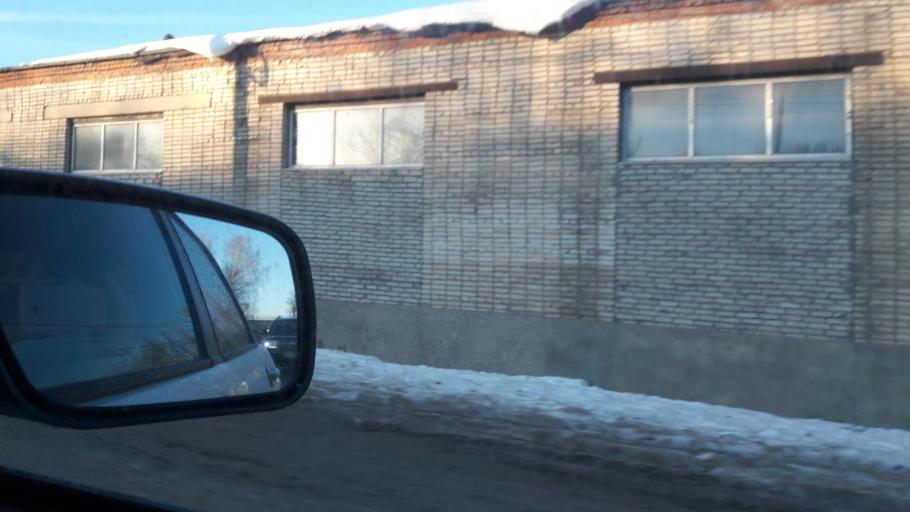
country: RU
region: Tula
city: Tula
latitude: 54.2170
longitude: 37.6471
